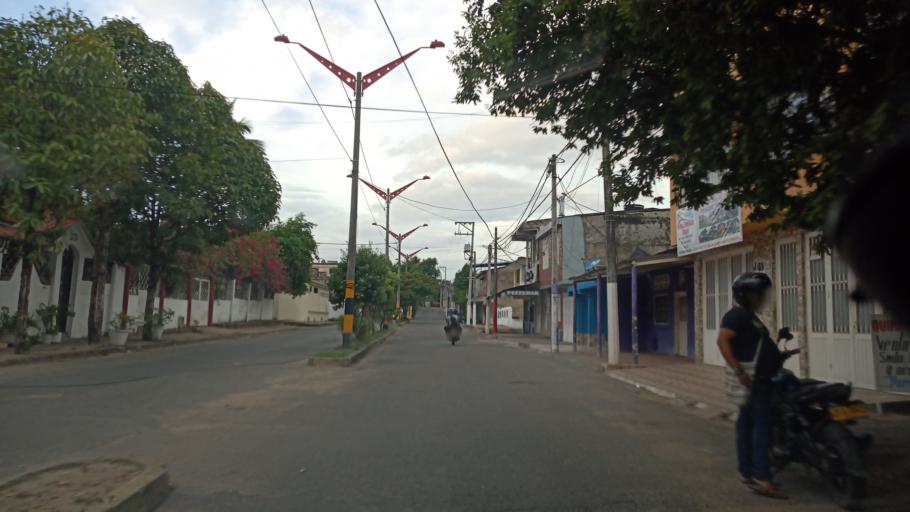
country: CO
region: Tolima
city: Melgar
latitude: 4.1995
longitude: -74.6503
